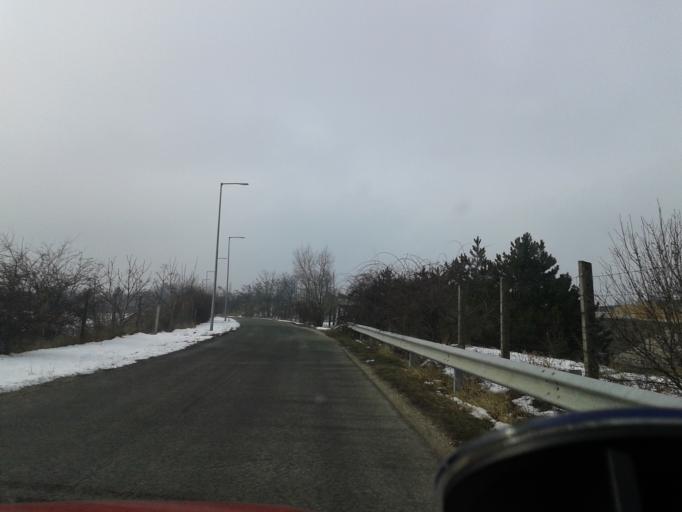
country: HU
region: Pest
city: Diosd
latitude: 47.4188
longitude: 18.9364
